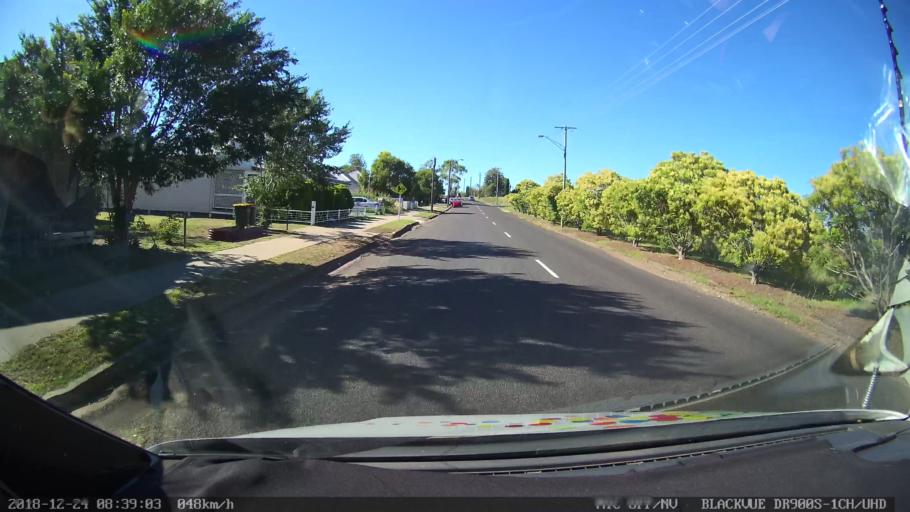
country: AU
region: New South Wales
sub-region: Liverpool Plains
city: Quirindi
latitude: -31.3452
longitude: 150.6474
